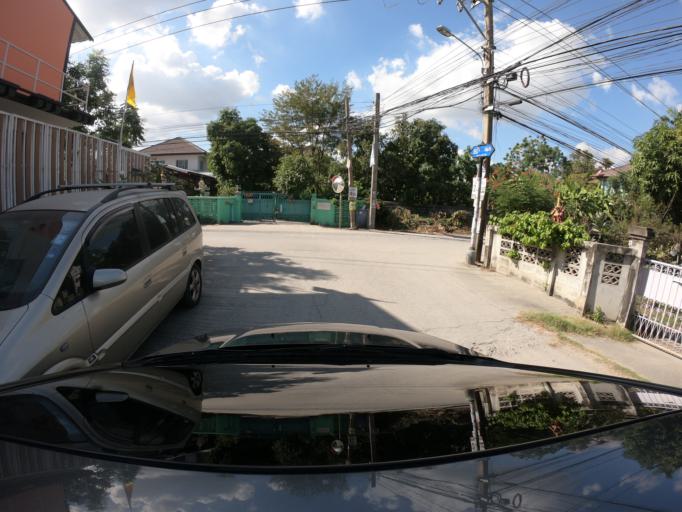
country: TH
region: Bangkok
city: Bang Na
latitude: 13.6529
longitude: 100.6237
